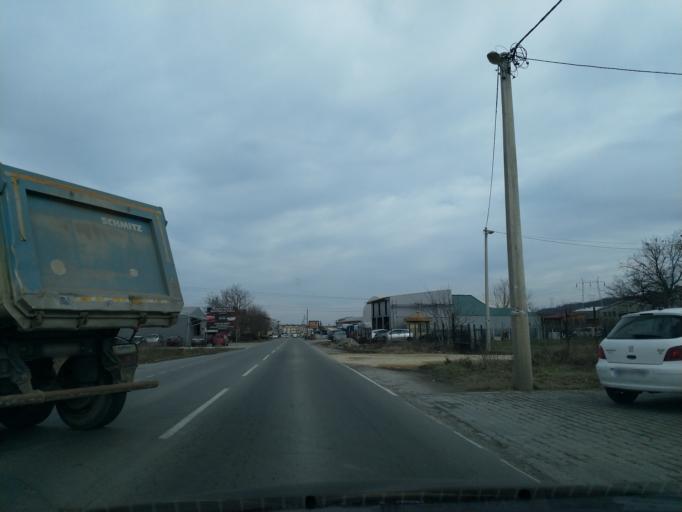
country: RS
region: Central Serbia
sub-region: Belgrade
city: Zvezdara
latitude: 44.7409
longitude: 20.5961
